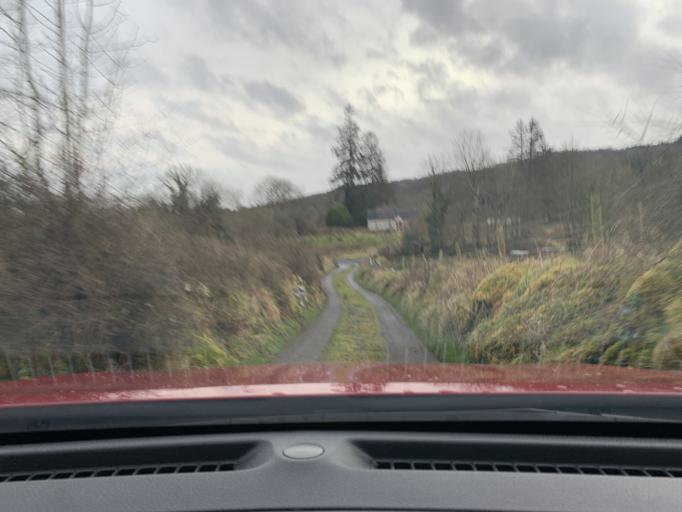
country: IE
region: Connaught
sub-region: Sligo
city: Ballymote
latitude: 53.9706
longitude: -8.4727
